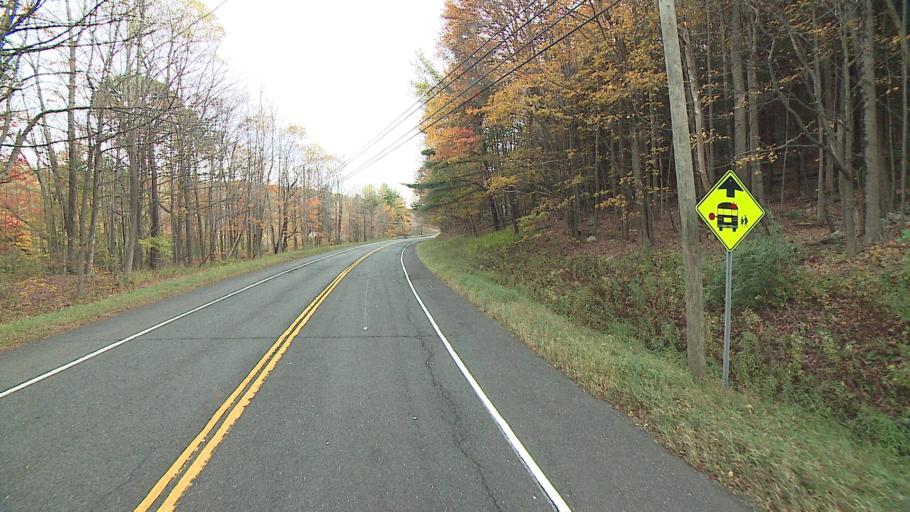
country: US
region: Connecticut
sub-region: Litchfield County
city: Winchester Center
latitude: 41.9599
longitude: -73.1198
